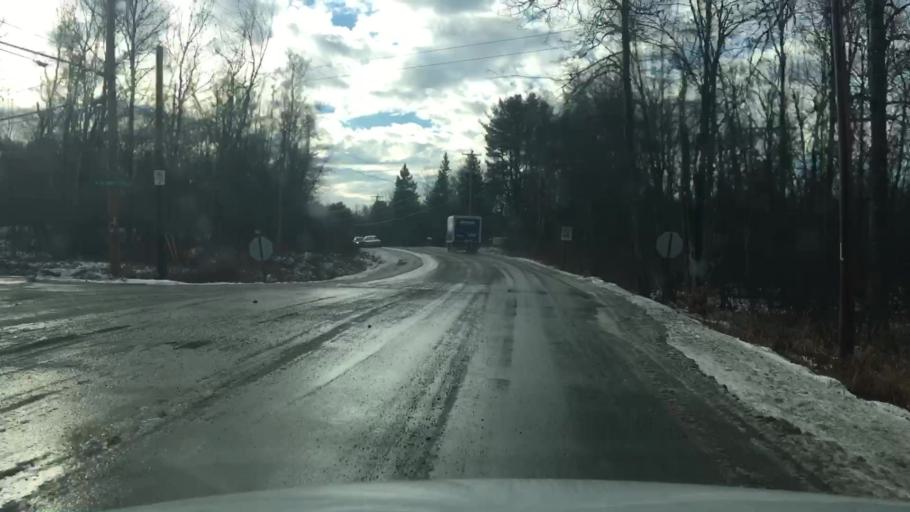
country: US
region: Maine
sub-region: Penobscot County
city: Brewer
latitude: 44.7280
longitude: -68.7557
